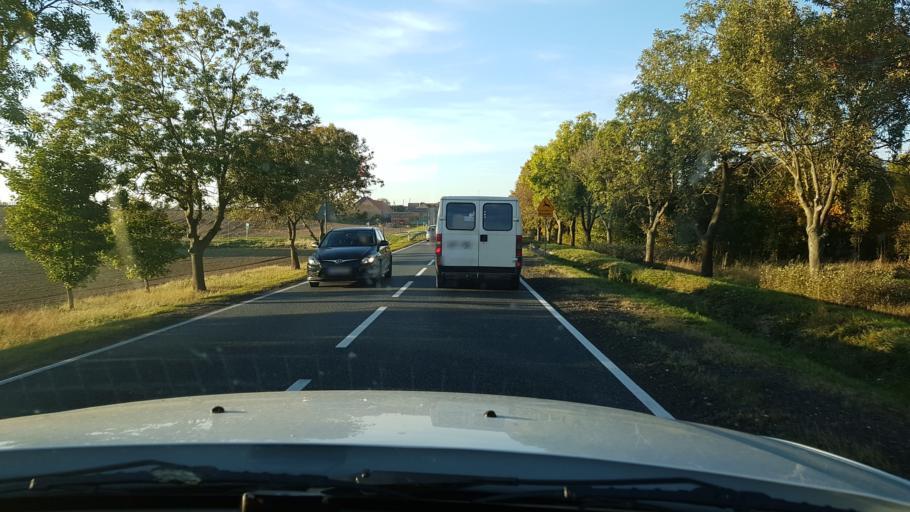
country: DE
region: Brandenburg
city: Schwedt (Oder)
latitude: 53.0243
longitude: 14.3249
